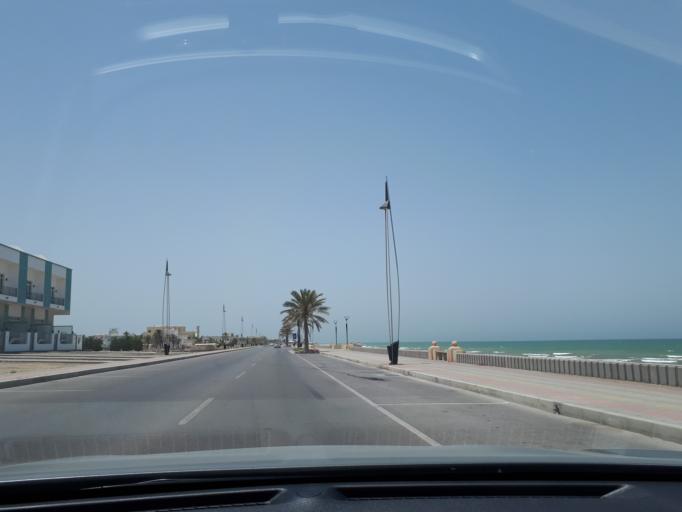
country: OM
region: Muhafazat Masqat
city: As Sib al Jadidah
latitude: 23.6616
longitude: 58.2190
